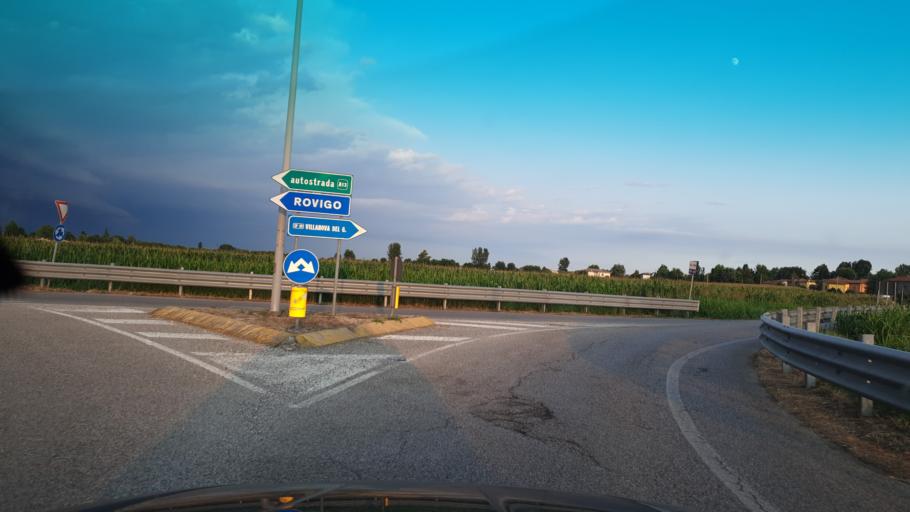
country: IT
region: Veneto
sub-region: Provincia di Rovigo
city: Lendinara
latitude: 45.0771
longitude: 11.6111
